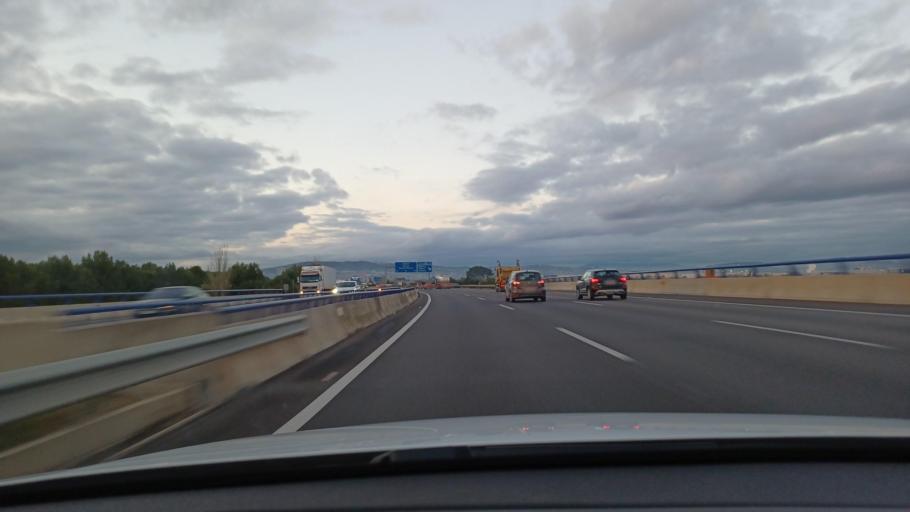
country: ES
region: Valencia
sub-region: Provincia de Valencia
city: Ribarroja
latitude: 39.4904
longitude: -0.5380
